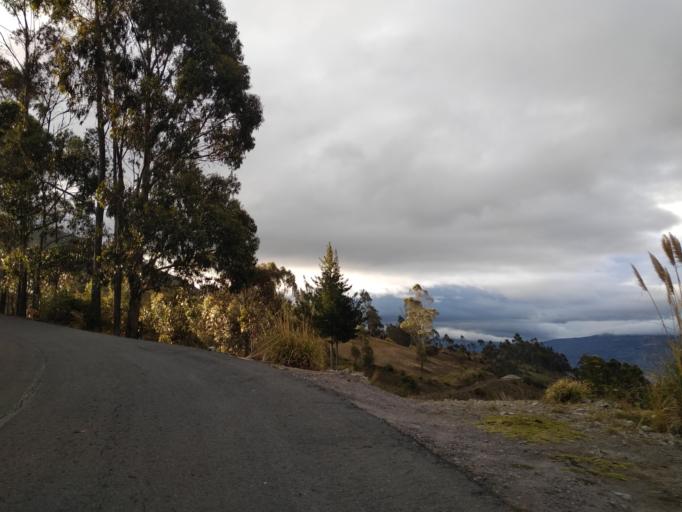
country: EC
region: Chimborazo
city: Riobamba
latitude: -1.6995
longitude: -78.7088
